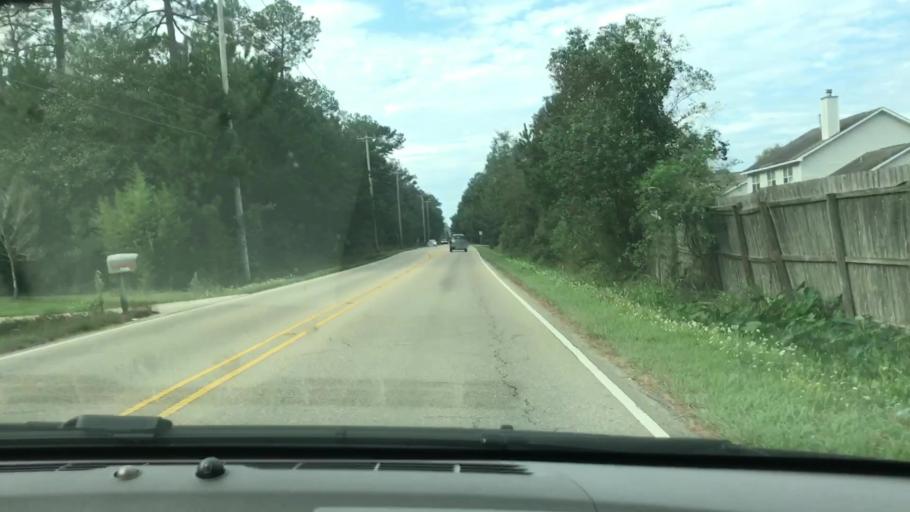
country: US
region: Louisiana
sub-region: Saint Tammany Parish
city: Abita Springs
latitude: 30.4600
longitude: -90.0454
